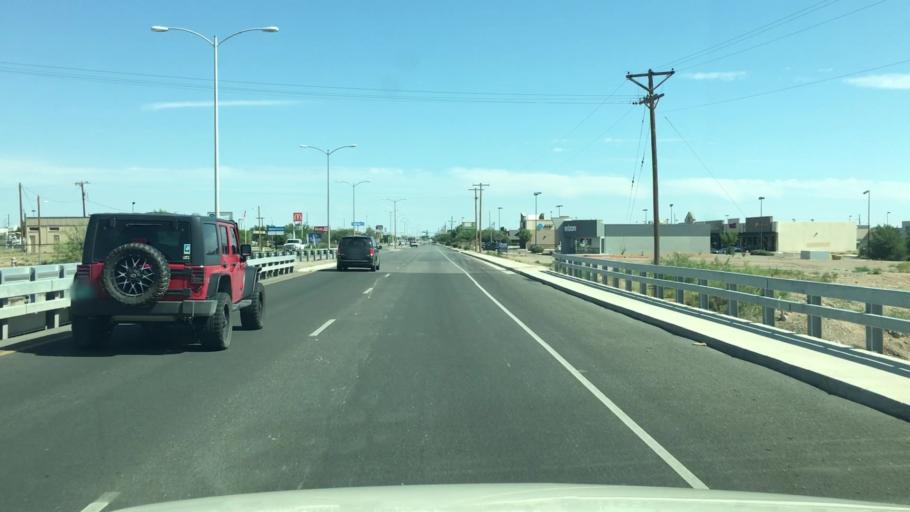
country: US
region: New Mexico
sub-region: Chaves County
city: Roswell
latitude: 33.4448
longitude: -104.5232
